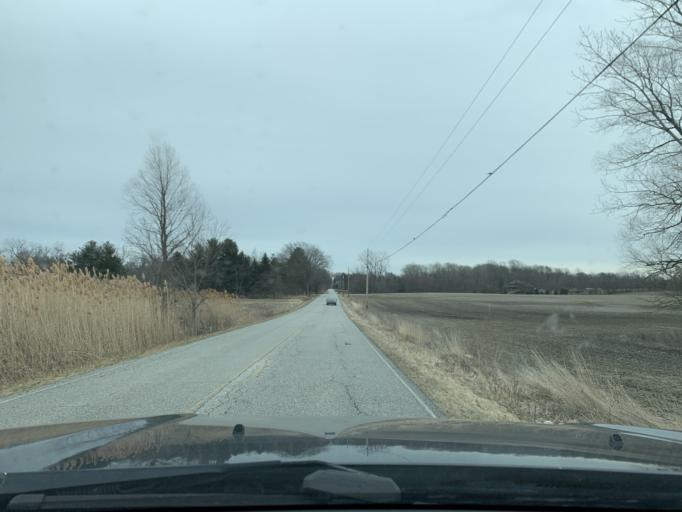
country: US
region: Indiana
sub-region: Porter County
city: Chesterton
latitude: 41.5859
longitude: -87.0134
